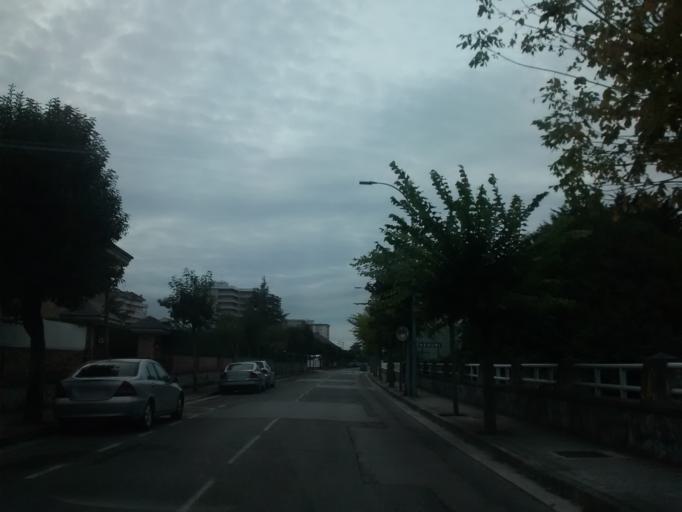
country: ES
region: Cantabria
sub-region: Provincia de Cantabria
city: Laredo
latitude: 43.4108
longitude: -3.4316
